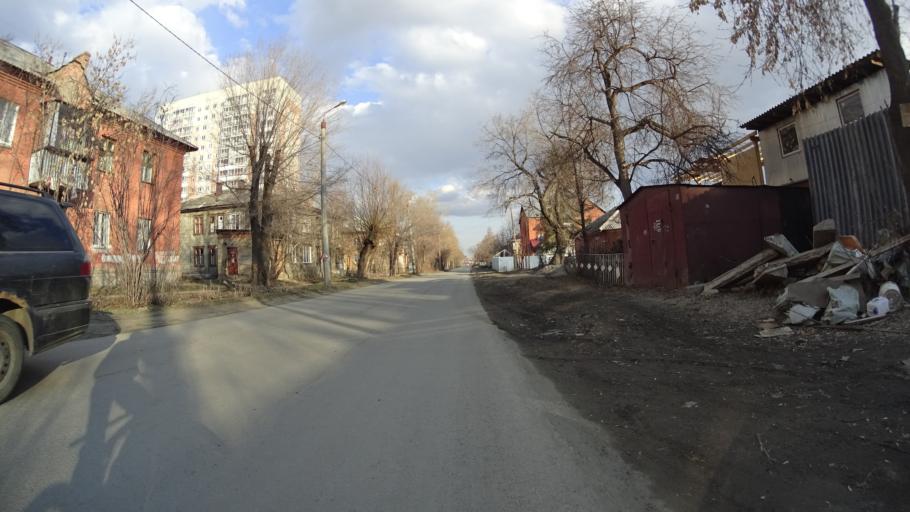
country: RU
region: Chelyabinsk
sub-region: Gorod Chelyabinsk
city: Chelyabinsk
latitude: 55.1410
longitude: 61.3867
